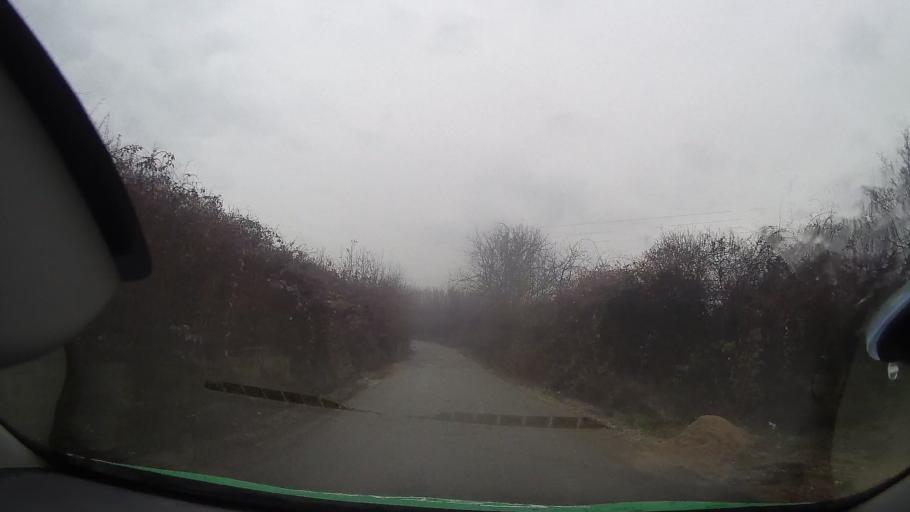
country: RO
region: Bihor
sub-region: Comuna Uileacu de Beius
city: Uileacu de Beius
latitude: 46.6874
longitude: 22.2215
